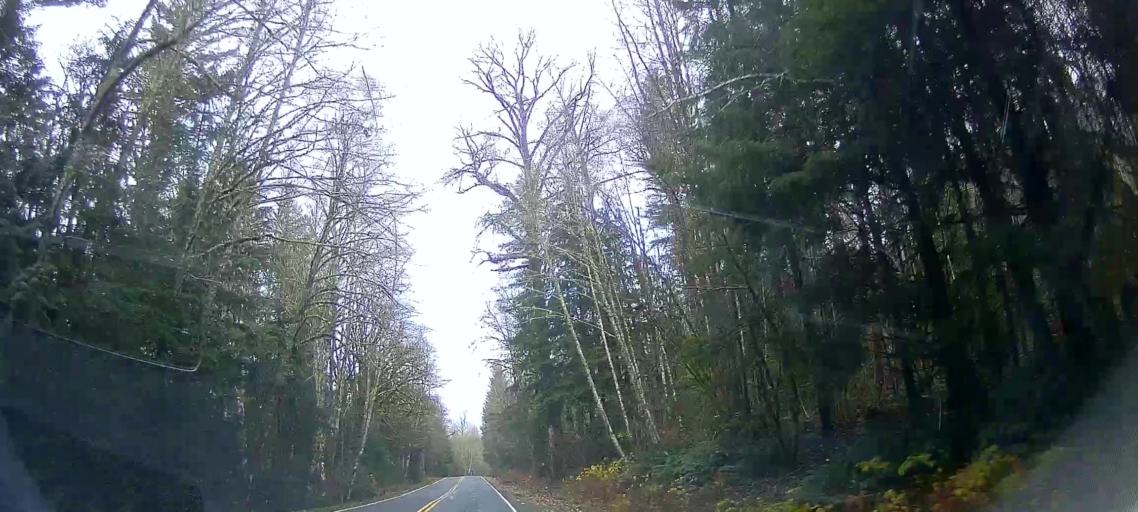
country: US
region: Washington
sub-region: Snohomish County
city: Darrington
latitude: 48.4923
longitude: -121.4741
